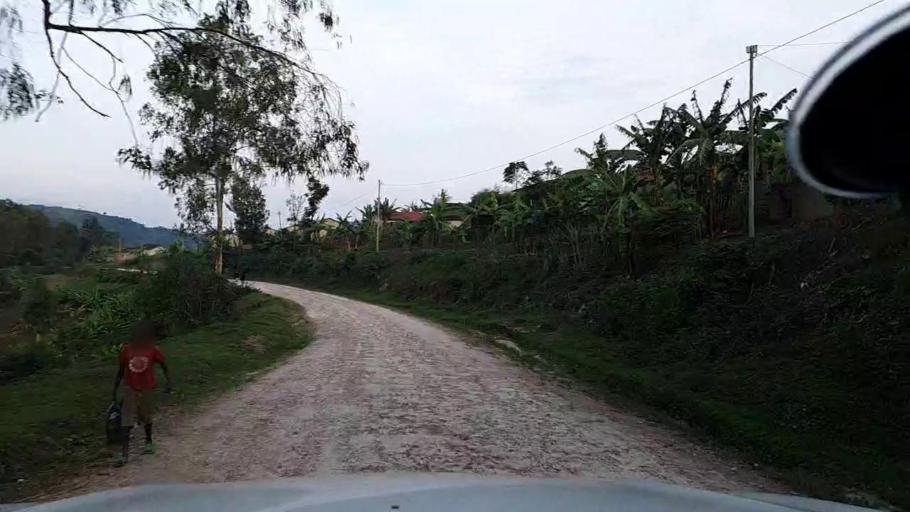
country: RW
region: Southern Province
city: Nyanza
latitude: -2.2158
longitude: 29.6368
